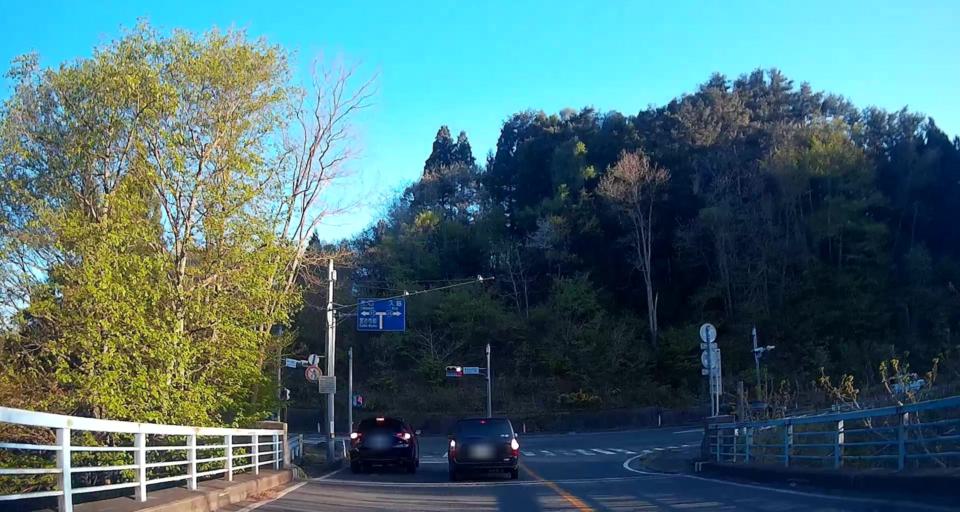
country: JP
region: Iwate
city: Miyako
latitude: 39.6506
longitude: 141.9603
